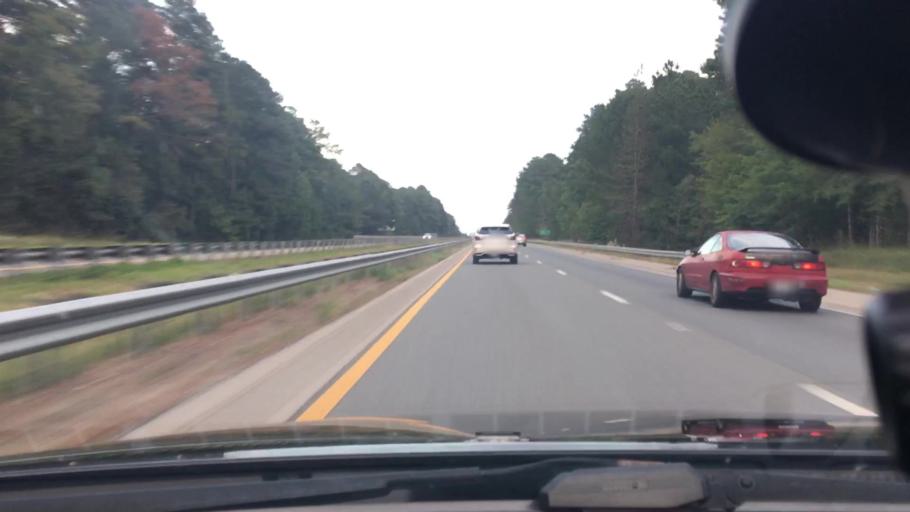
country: US
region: North Carolina
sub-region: Chatham County
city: Pittsboro
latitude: 35.6284
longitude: -79.0751
